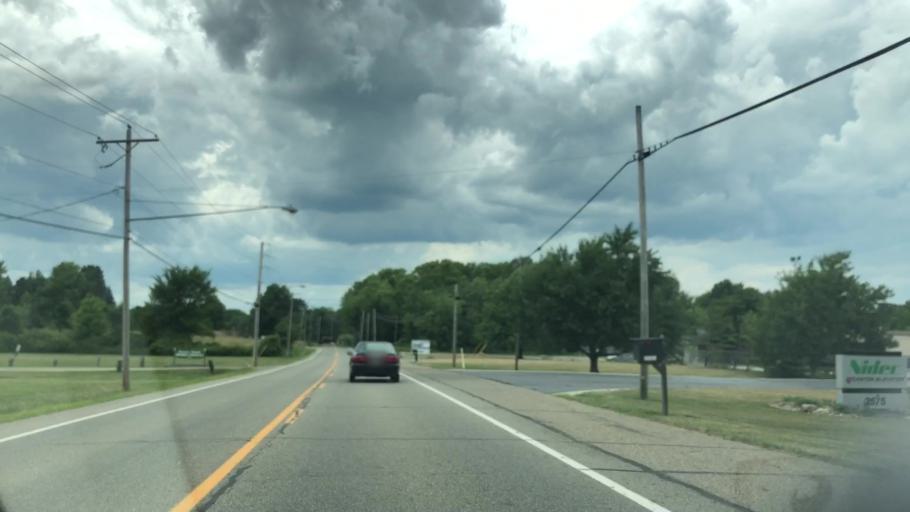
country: US
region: Ohio
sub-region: Summit County
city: Greensburg
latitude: 40.9305
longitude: -81.4535
